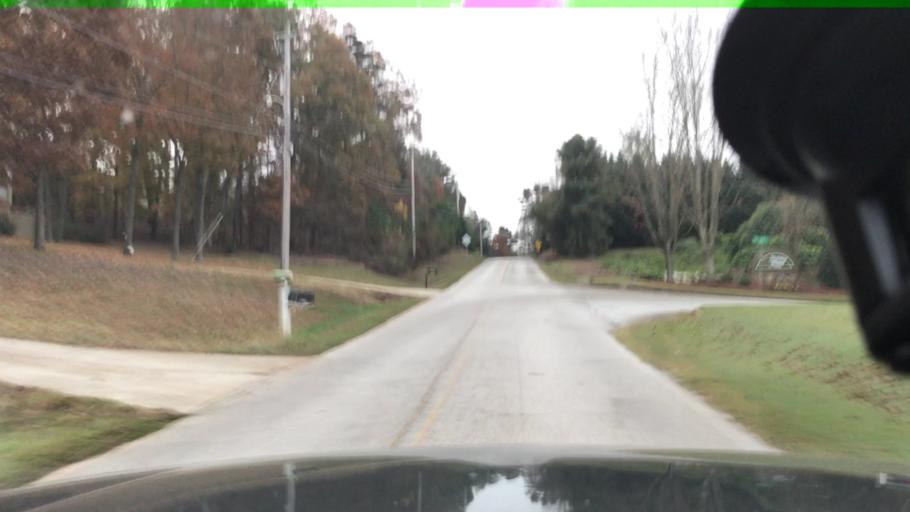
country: US
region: Georgia
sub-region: Gwinnett County
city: Buford
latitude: 34.1572
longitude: -83.9934
